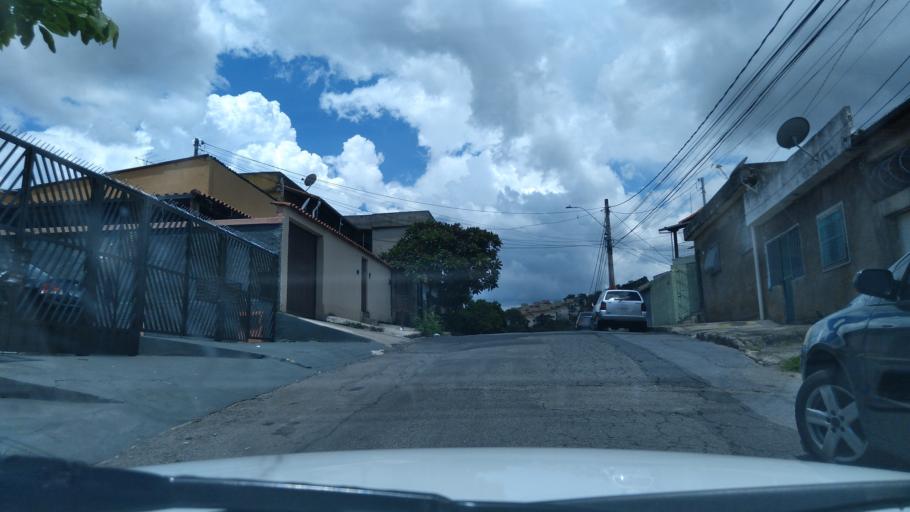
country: BR
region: Minas Gerais
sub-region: Belo Horizonte
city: Belo Horizonte
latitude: -19.8625
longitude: -43.8971
